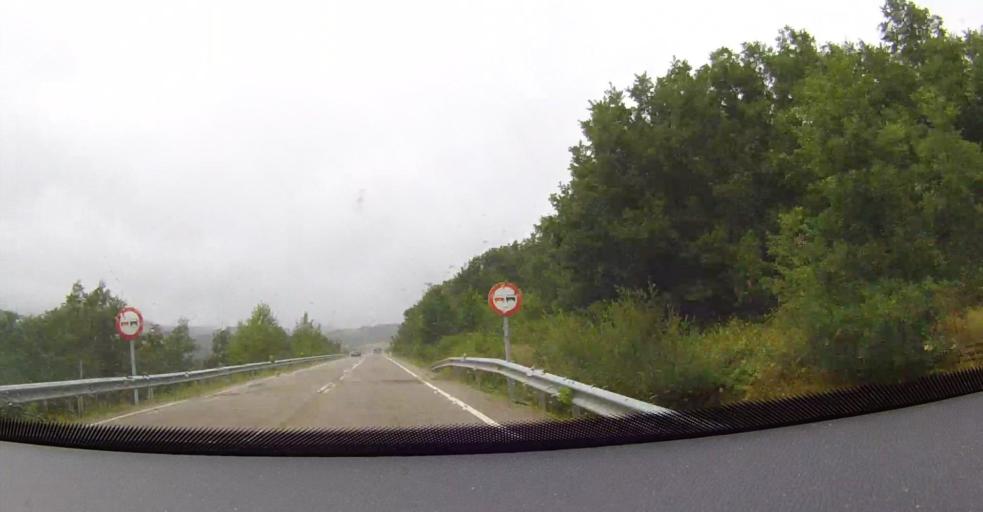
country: ES
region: Castille and Leon
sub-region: Provincia de Leon
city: Sabero
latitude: 42.8389
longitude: -5.2362
